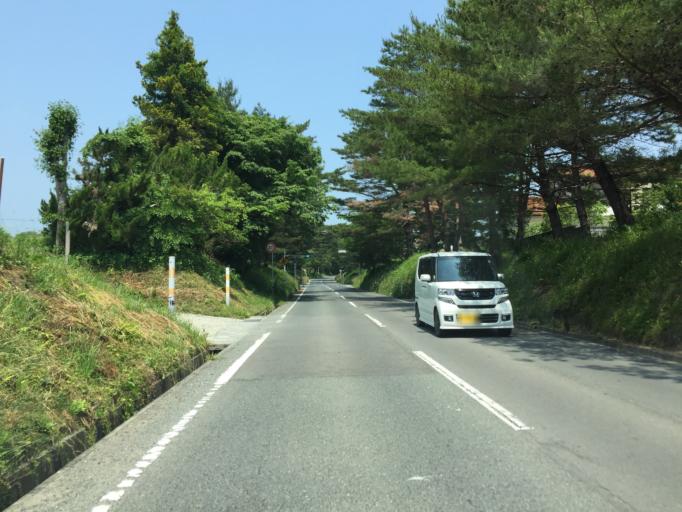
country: JP
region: Miyagi
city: Marumori
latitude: 37.7706
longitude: 140.9376
